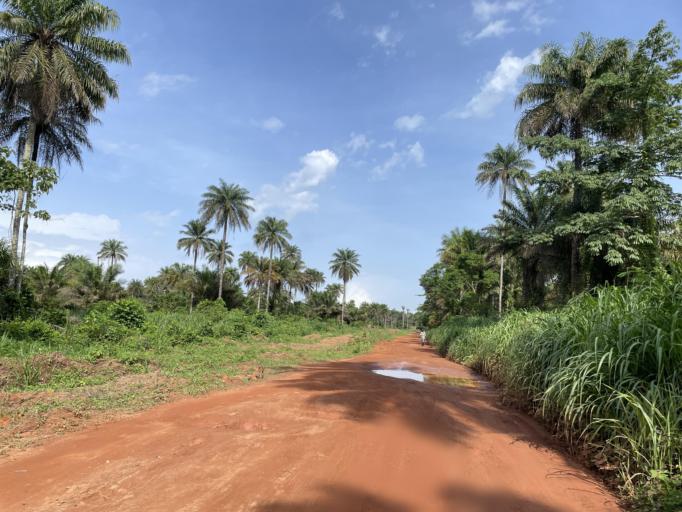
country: SL
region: Southern Province
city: Pujehun
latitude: 7.3715
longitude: -11.7436
